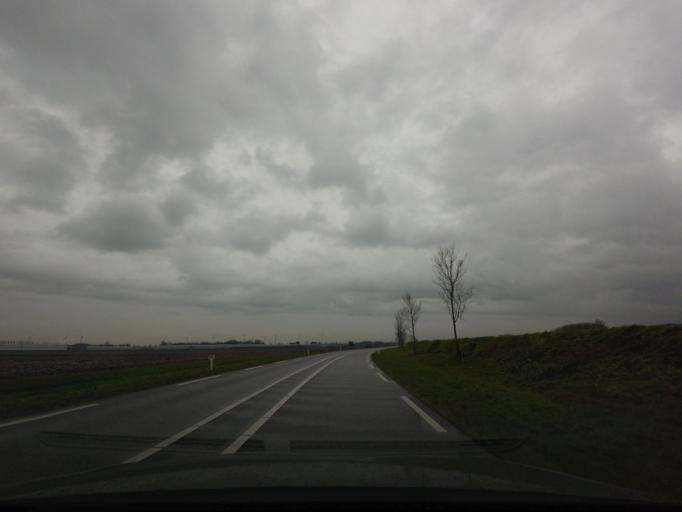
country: NL
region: North Brabant
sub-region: Gemeente Moerdijk
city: Klundert
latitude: 51.6412
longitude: 4.6250
